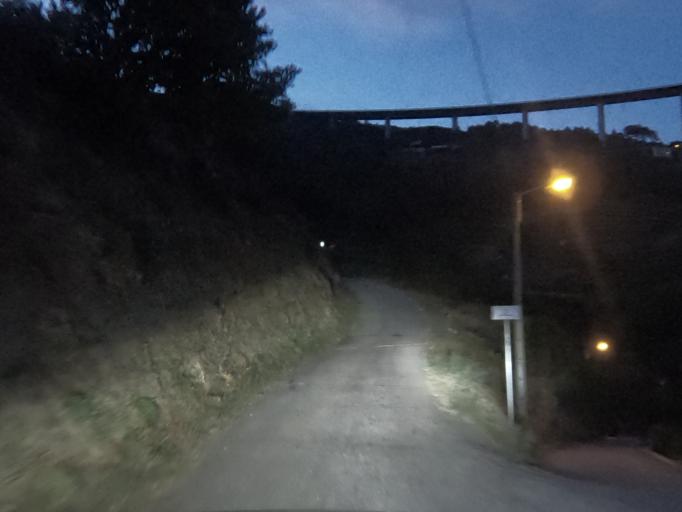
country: PT
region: Vila Real
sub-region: Vila Real
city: Vila Real
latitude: 41.2739
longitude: -7.7613
